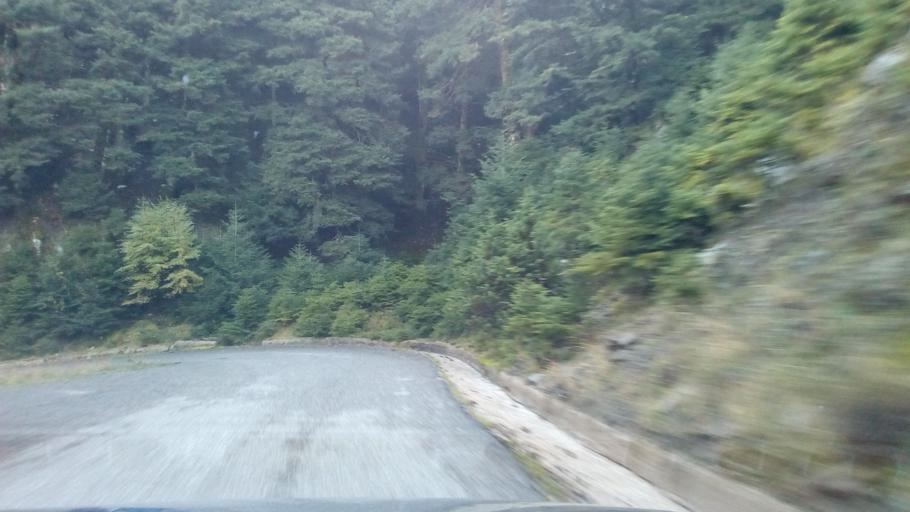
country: GR
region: West Greece
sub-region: Nomos Aitolias kai Akarnanias
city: Nafpaktos
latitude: 38.5348
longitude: 21.8459
